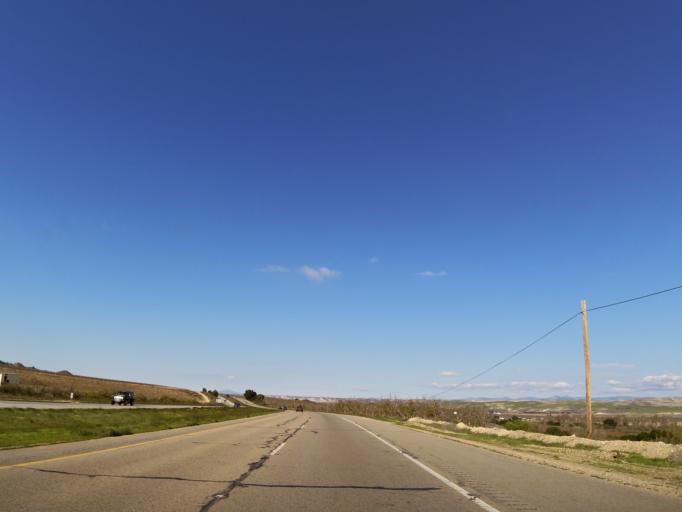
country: US
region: California
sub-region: San Luis Obispo County
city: Lake Nacimiento
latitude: 35.9849
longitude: -120.9029
